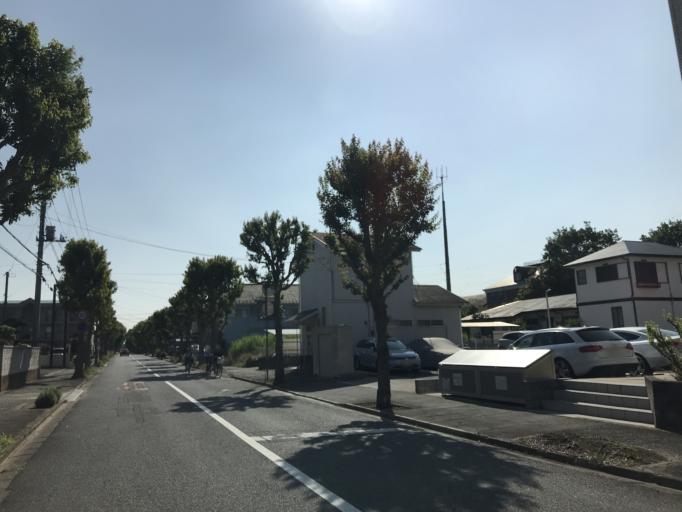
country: JP
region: Ibaraki
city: Naka
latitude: 36.0541
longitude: 140.1347
